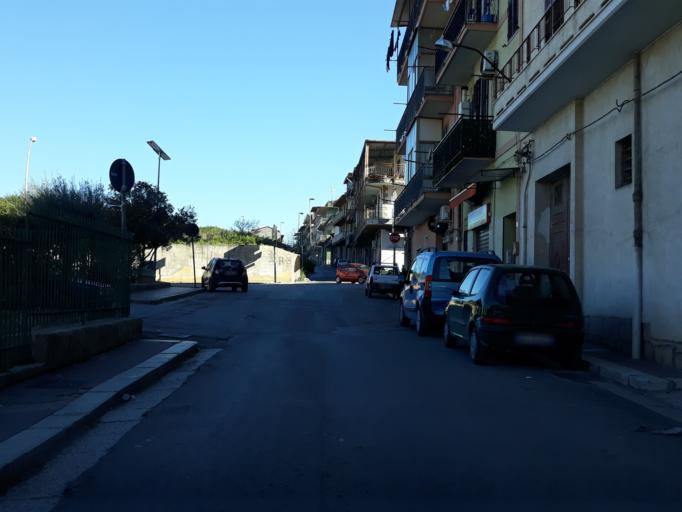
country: IT
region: Sicily
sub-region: Palermo
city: Misilmeri
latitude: 38.0293
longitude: 13.4490
